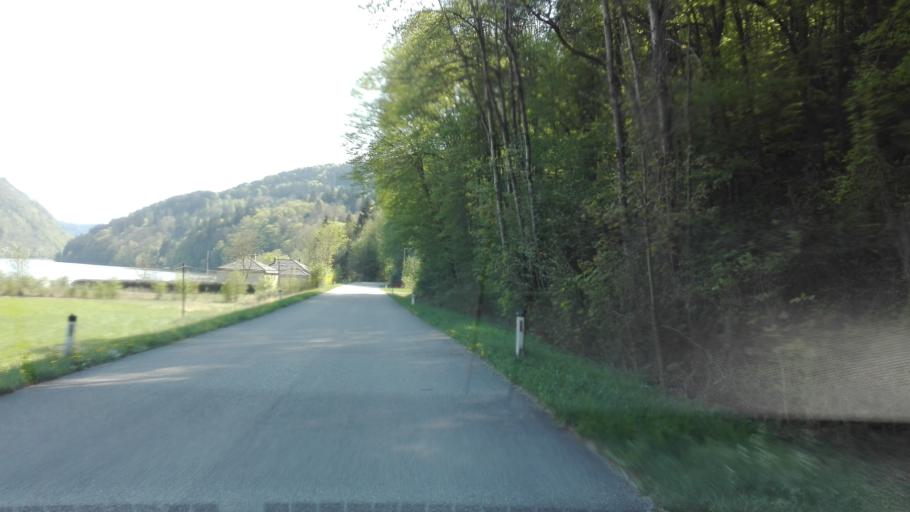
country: AT
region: Upper Austria
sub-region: Politischer Bezirk Rohrbach
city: Atzesberg
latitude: 48.4431
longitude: 13.9173
